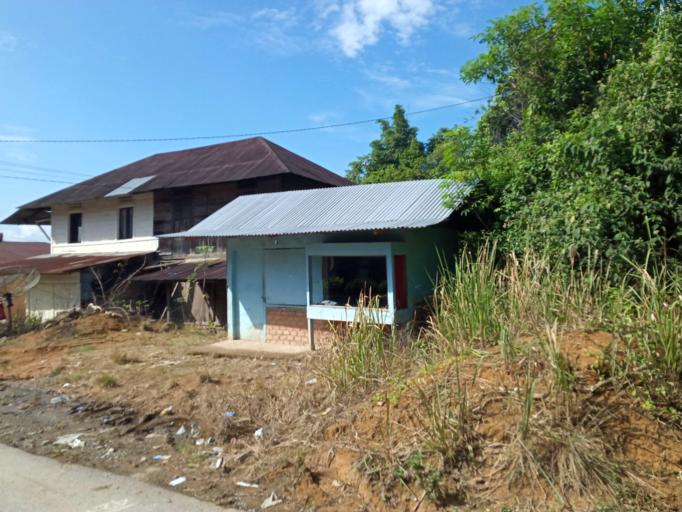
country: ID
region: Jambi
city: Sungai Penuh
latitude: -2.1642
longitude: 101.5914
